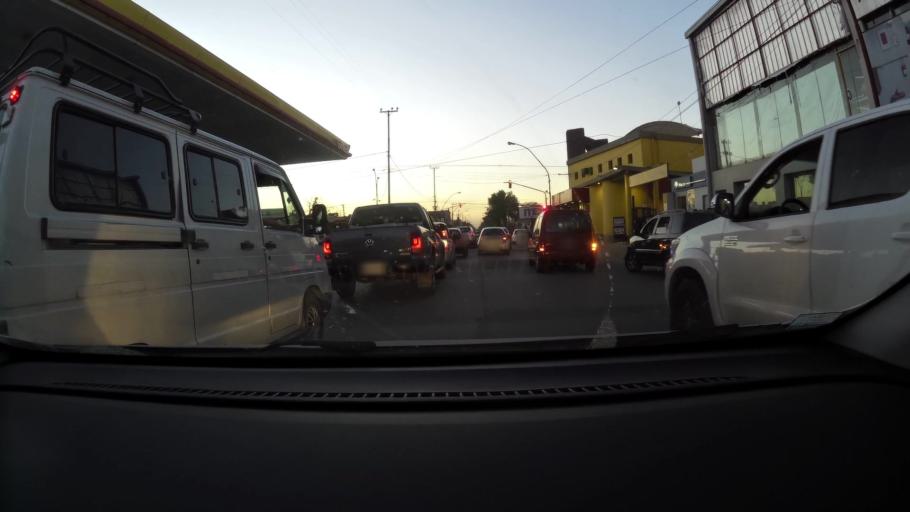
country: AR
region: Santa Fe
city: Santa Fe de la Vera Cruz
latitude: -31.6017
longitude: -60.7120
